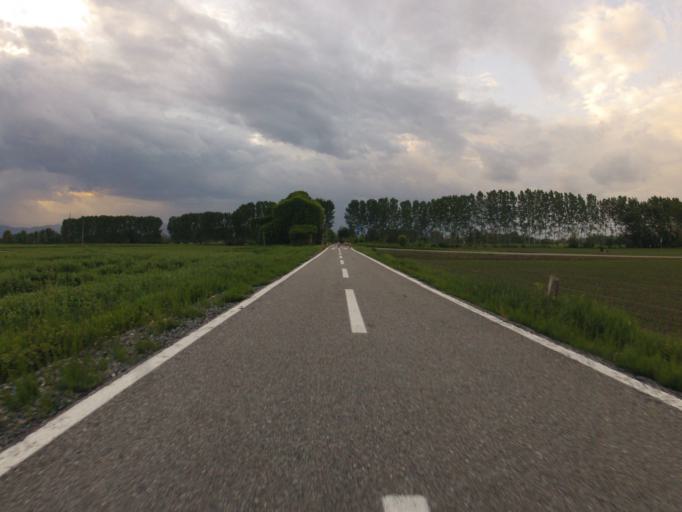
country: IT
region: Piedmont
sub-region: Provincia di Torino
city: Vigone
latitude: 44.8254
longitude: 7.4950
